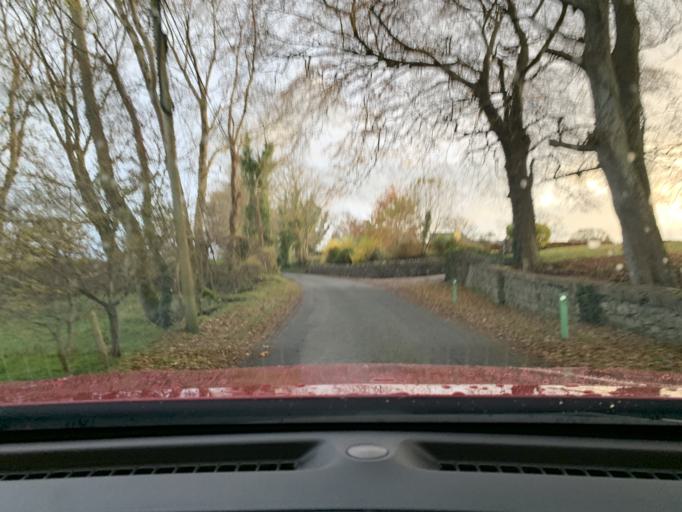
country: IE
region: Connaught
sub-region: Sligo
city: Sligo
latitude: 54.3012
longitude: -8.4921
